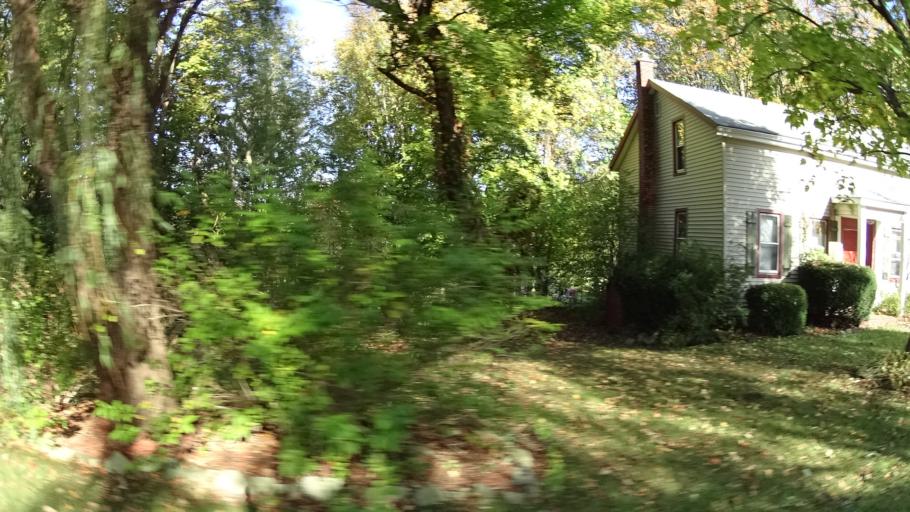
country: US
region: Ohio
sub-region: Lorain County
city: South Amherst
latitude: 41.3915
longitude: -82.2706
